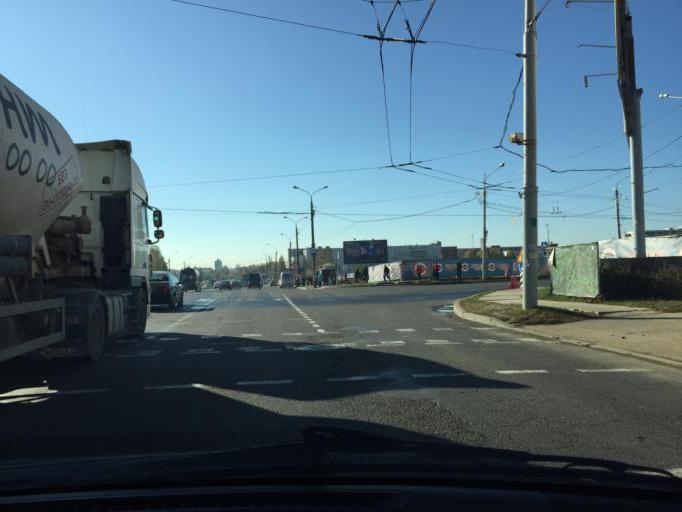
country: BY
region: Minsk
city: Syenitsa
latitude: 53.8440
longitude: 27.5342
